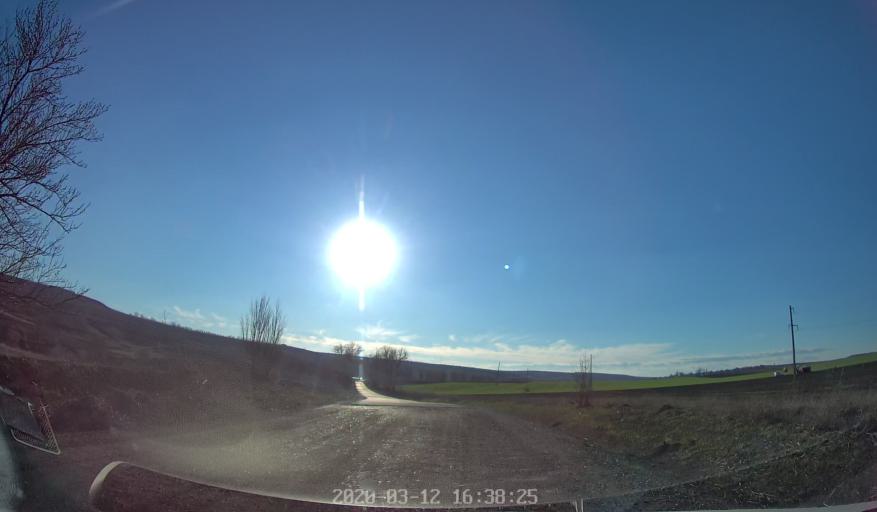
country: MD
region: Anenii Noi
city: Anenii Noi
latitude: 46.8156
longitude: 29.1789
